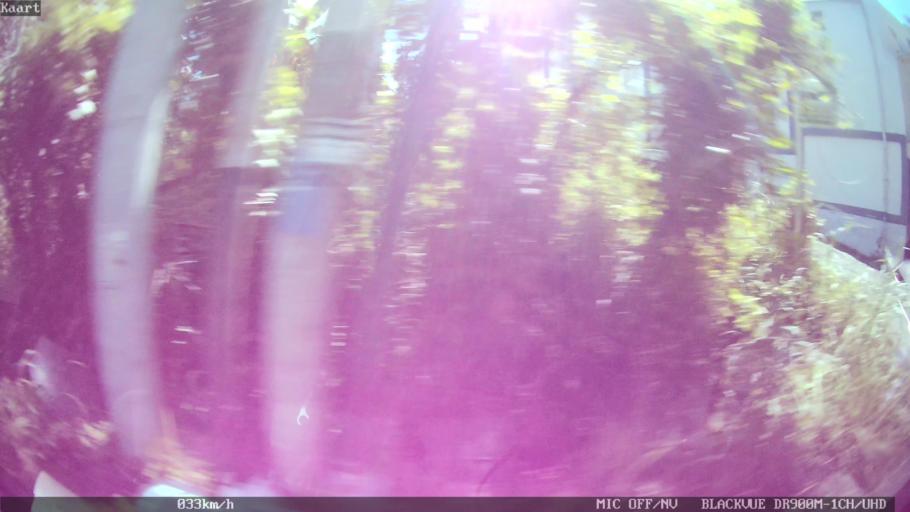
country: ID
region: Bali
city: Banjar Kelodan
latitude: -8.5330
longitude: 115.3352
